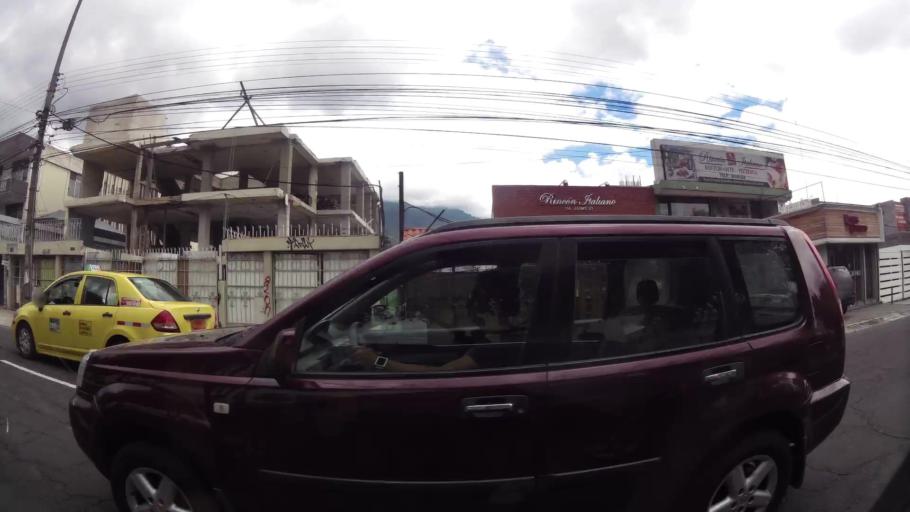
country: EC
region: Pichincha
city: Quito
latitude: -0.1684
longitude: -78.4796
